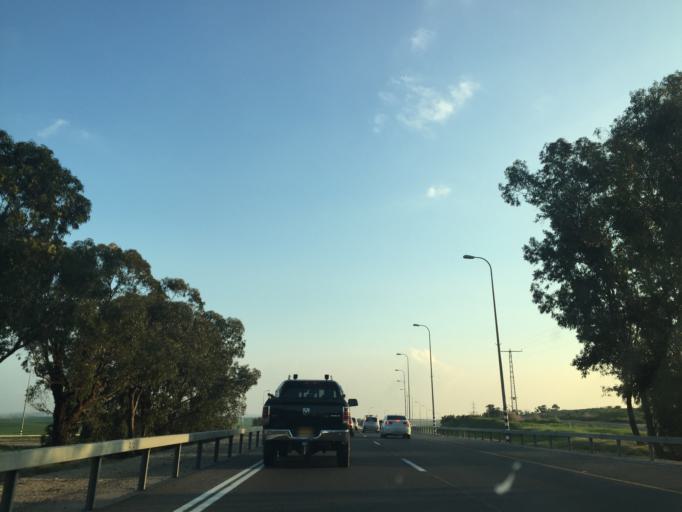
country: IL
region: Southern District
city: Lehavim
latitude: 31.4759
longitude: 34.7754
